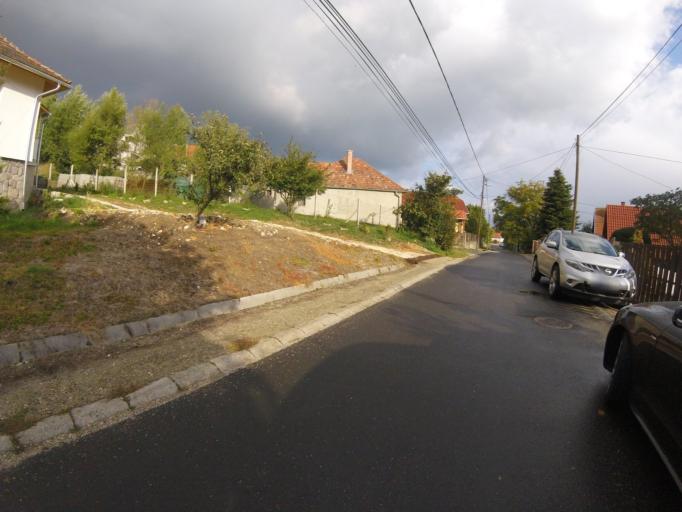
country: HU
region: Pest
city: Pilisszentkereszt
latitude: 47.6951
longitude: 18.8943
